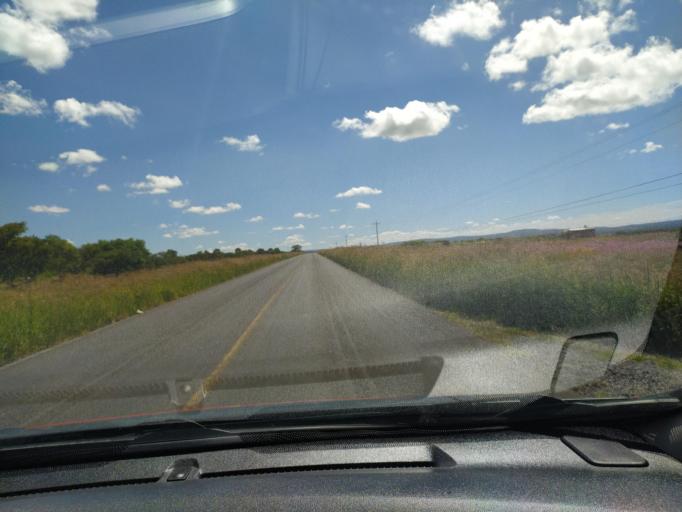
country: MX
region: Jalisco
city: Valle de Guadalupe
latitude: 21.0204
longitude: -102.5320
